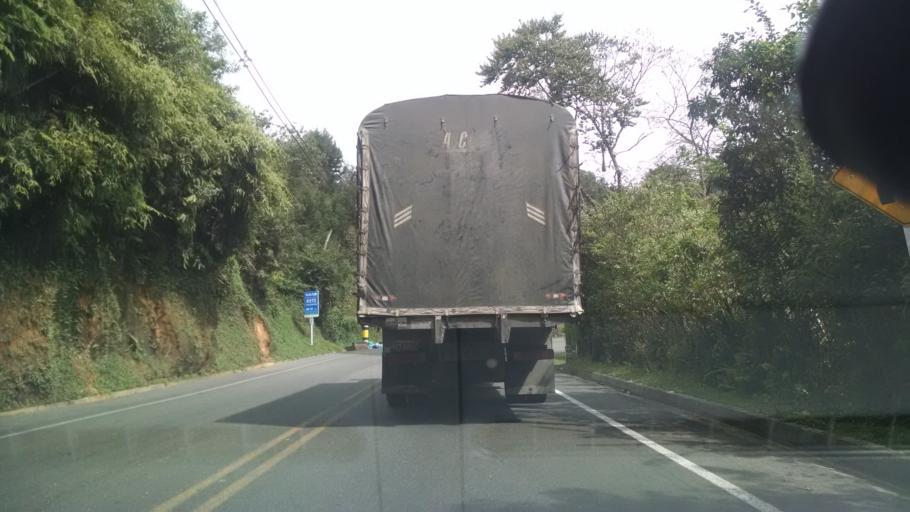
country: CO
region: Antioquia
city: Caldas
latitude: 6.0328
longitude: -75.6237
